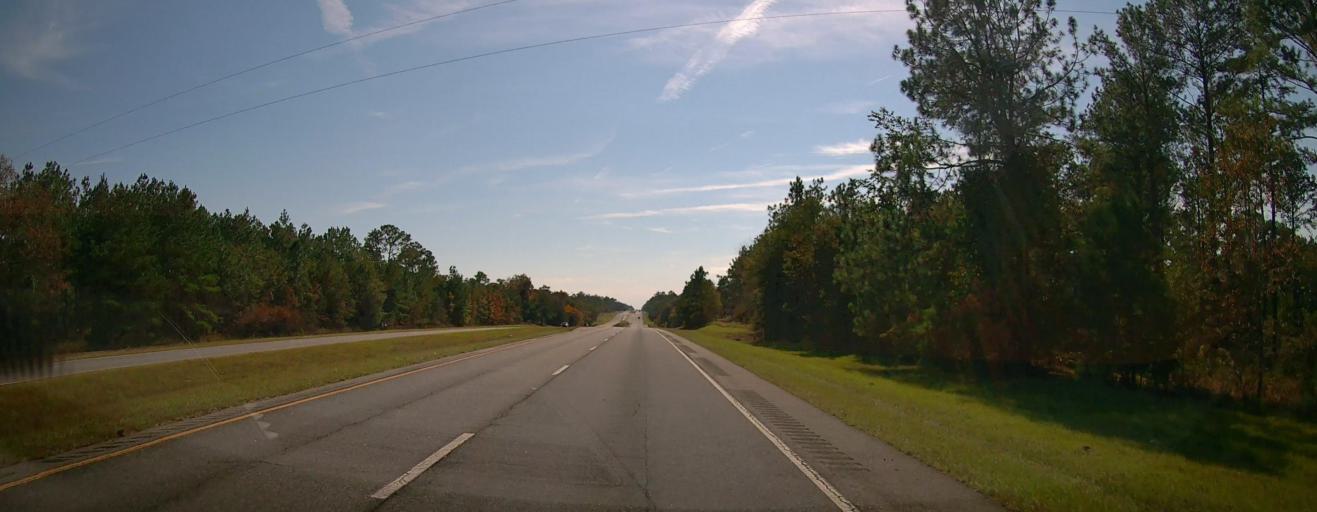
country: US
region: Georgia
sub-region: Lee County
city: Leesburg
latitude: 31.7232
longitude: -83.9878
